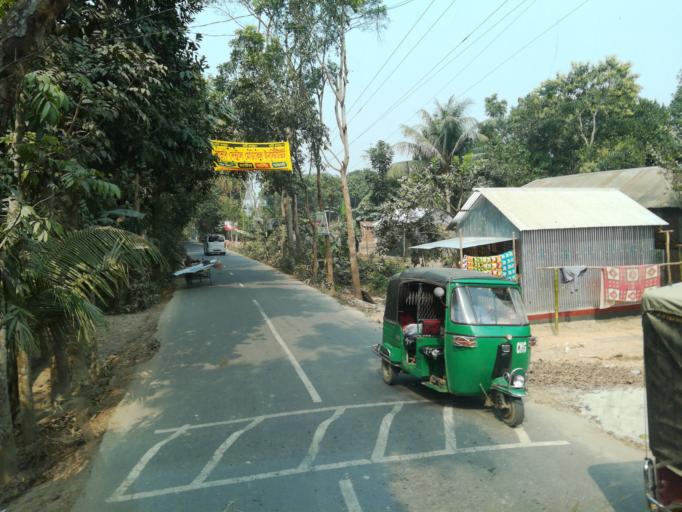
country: BD
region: Dhaka
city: Nagarpur
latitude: 24.0009
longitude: 89.8473
